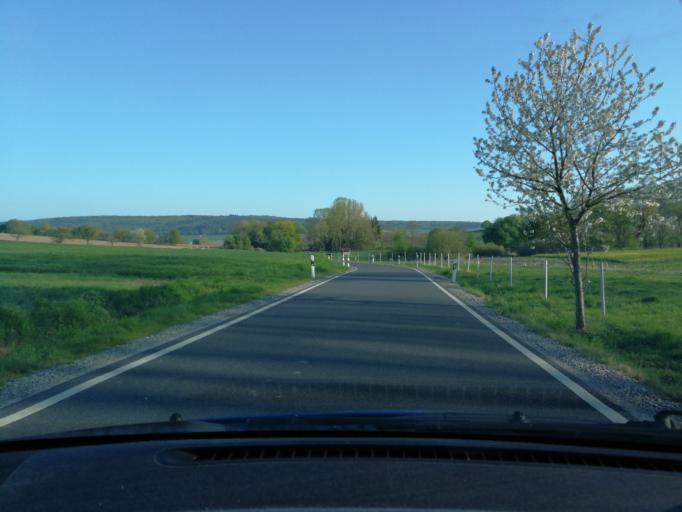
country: DE
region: Lower Saxony
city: Uslar
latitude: 51.5964
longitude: 9.6428
